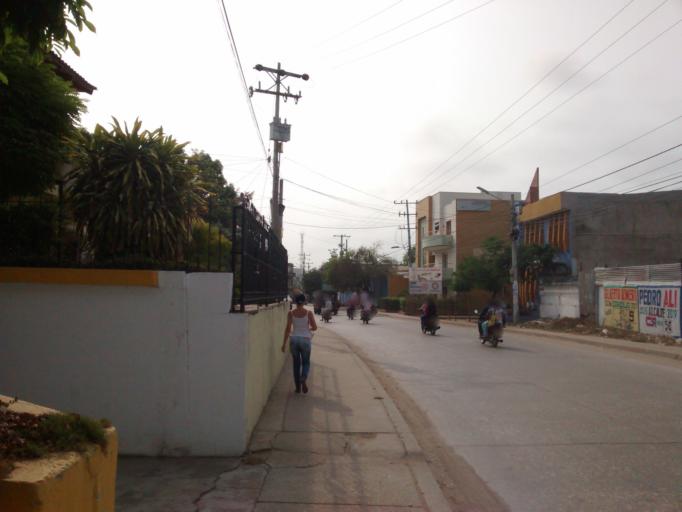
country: CO
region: Bolivar
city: Magangue
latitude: 9.2406
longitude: -74.7518
